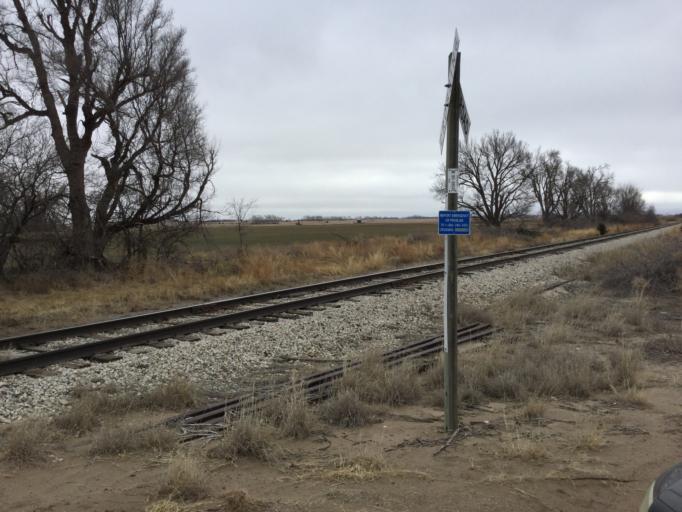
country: US
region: Kansas
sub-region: Barton County
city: Ellinwood
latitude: 38.3102
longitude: -98.4796
